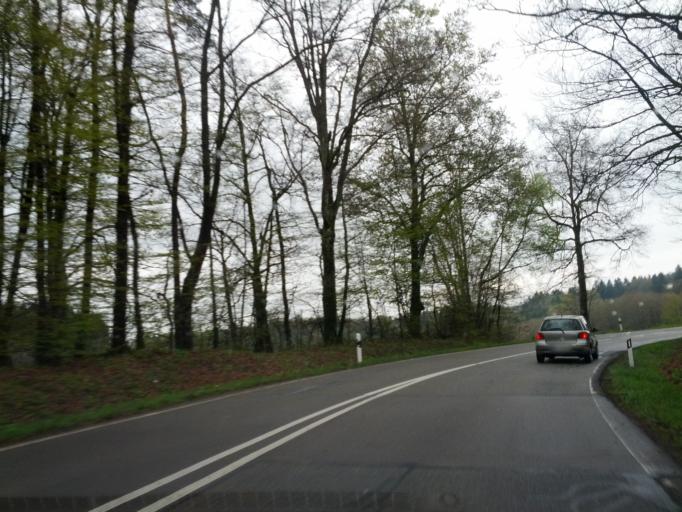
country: DE
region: Baden-Wuerttemberg
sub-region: Freiburg Region
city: Rickenbach
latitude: 47.6198
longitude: 8.0162
